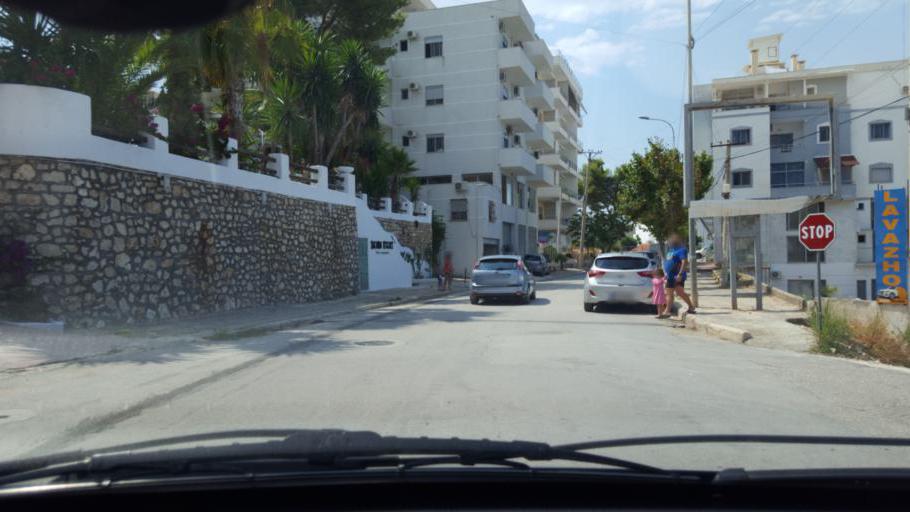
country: AL
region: Vlore
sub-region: Rrethi i Sarandes
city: Sarande
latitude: 39.8521
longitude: 20.0228
